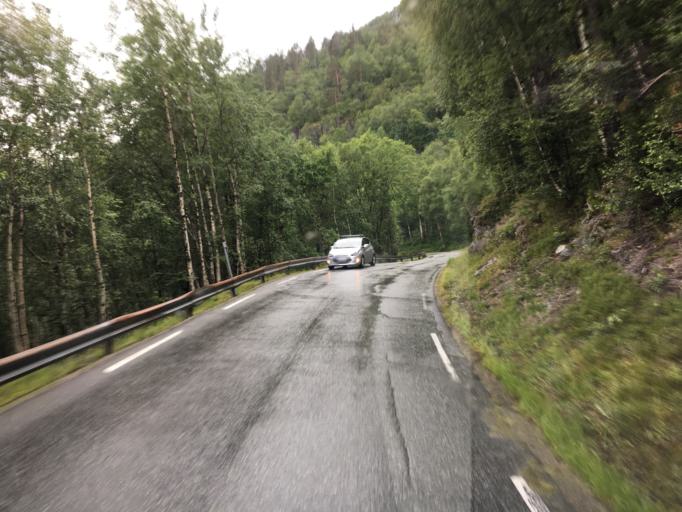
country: NO
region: Rogaland
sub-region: Sauda
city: Sauda
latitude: 59.6755
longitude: 6.4980
